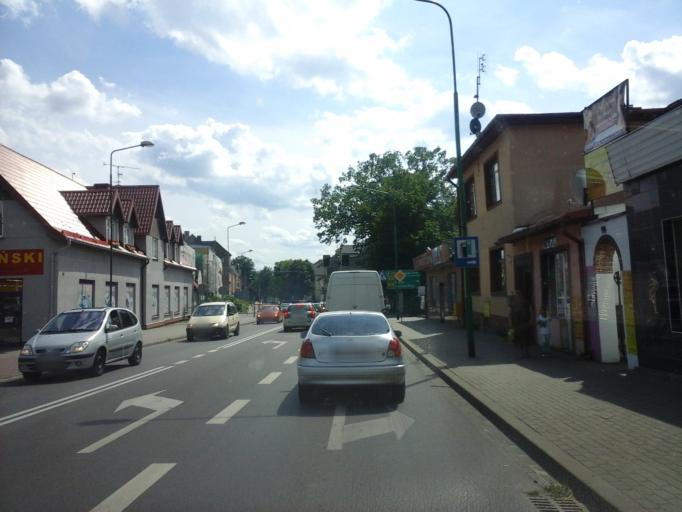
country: PL
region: West Pomeranian Voivodeship
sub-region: Powiat swidwinski
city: Swidwin
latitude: 53.7726
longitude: 15.7752
